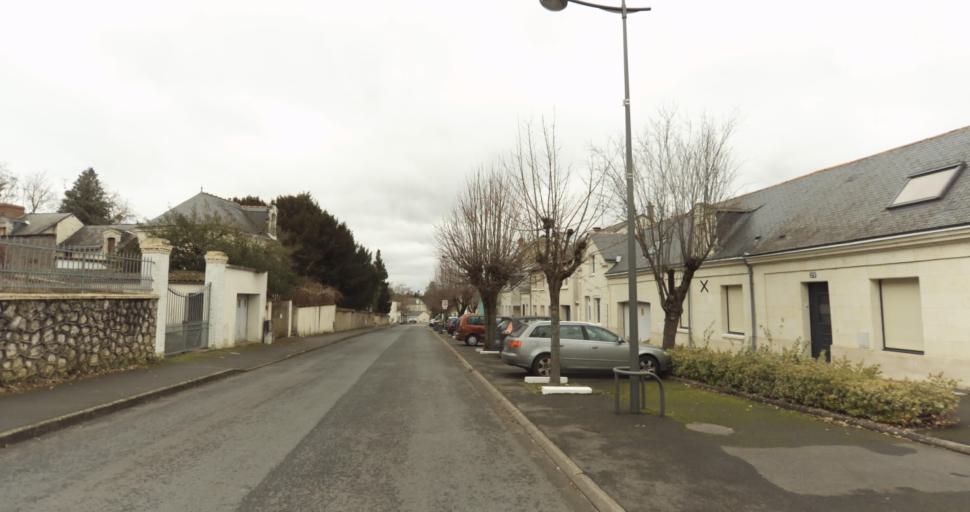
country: FR
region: Pays de la Loire
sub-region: Departement de Maine-et-Loire
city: Jumelles
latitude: 47.3795
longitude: -0.1073
